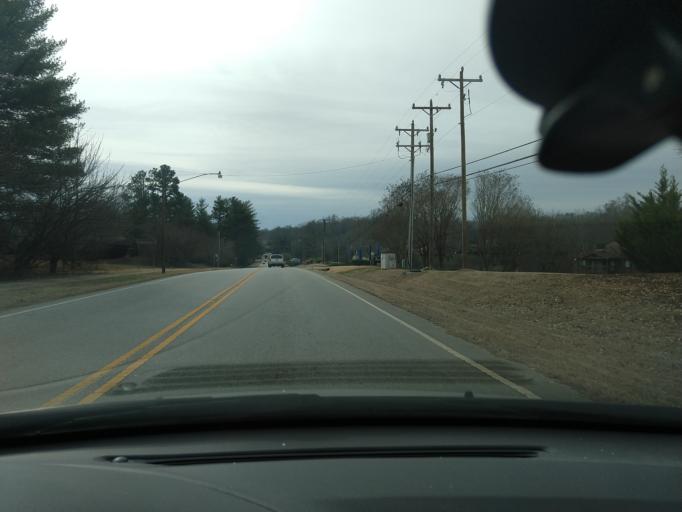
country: US
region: South Carolina
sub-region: Spartanburg County
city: Spartanburg
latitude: 34.9637
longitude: -81.9091
